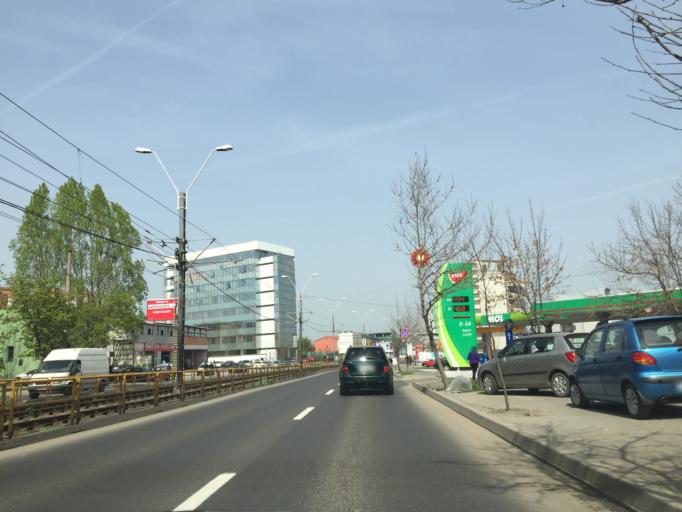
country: RO
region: Ilfov
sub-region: Comuna Chiajna
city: Rosu
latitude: 44.4412
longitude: 26.0356
